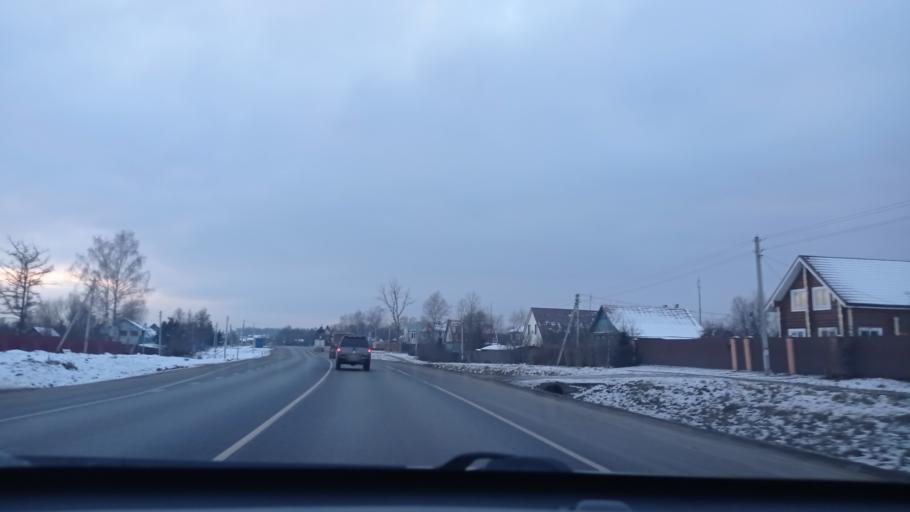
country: RU
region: Moskovskaya
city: Ateptsevo
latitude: 55.2008
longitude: 36.9243
